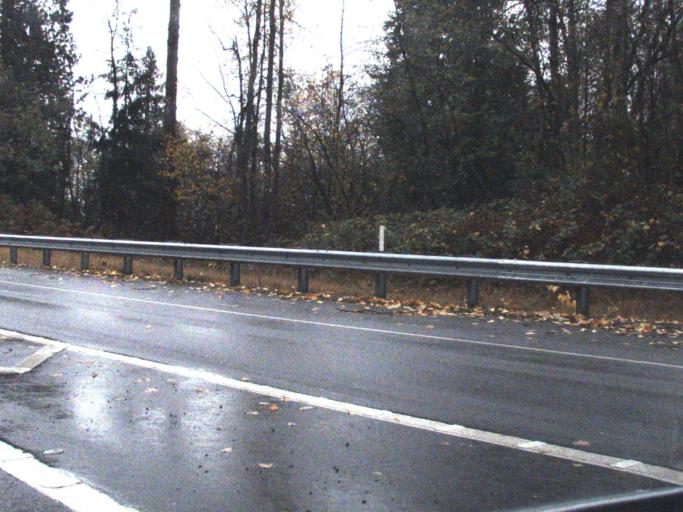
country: US
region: Washington
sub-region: Snohomish County
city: Fobes Hill
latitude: 47.9561
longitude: -122.1174
